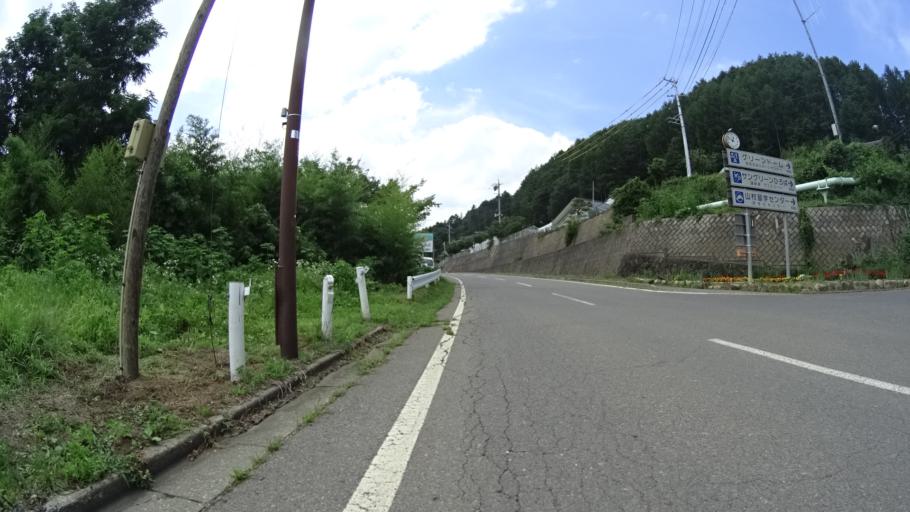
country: JP
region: Nagano
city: Saku
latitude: 36.0605
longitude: 138.5389
